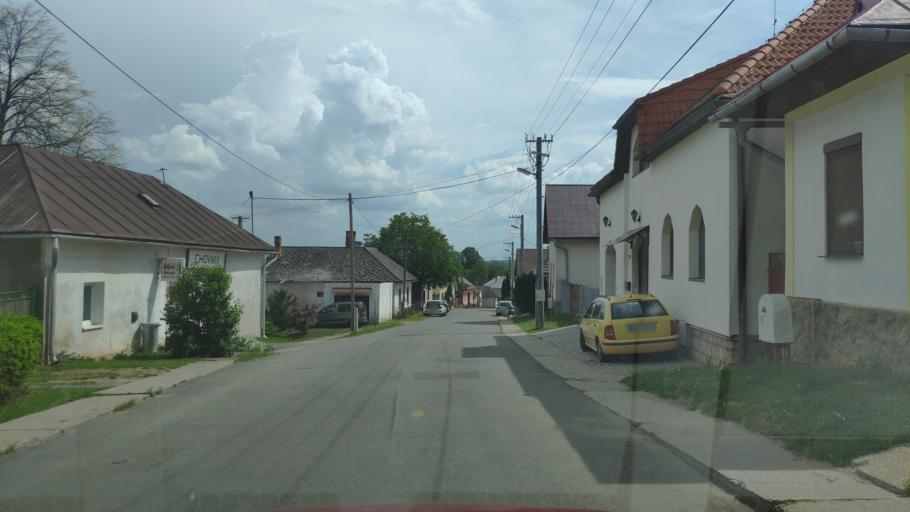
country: SK
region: Kosicky
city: Medzev
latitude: 48.7103
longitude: 20.9744
